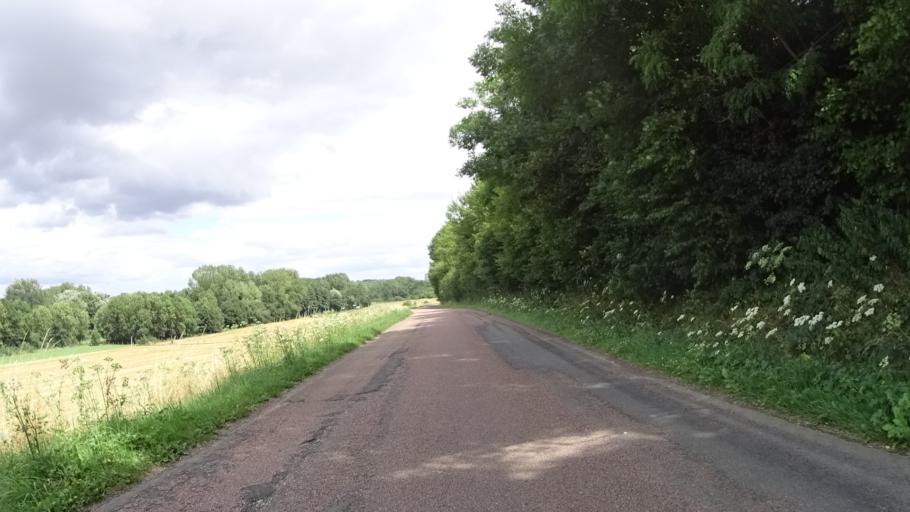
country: FR
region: Centre
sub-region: Departement du Loiret
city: Douchy
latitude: 47.9377
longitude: 3.0258
